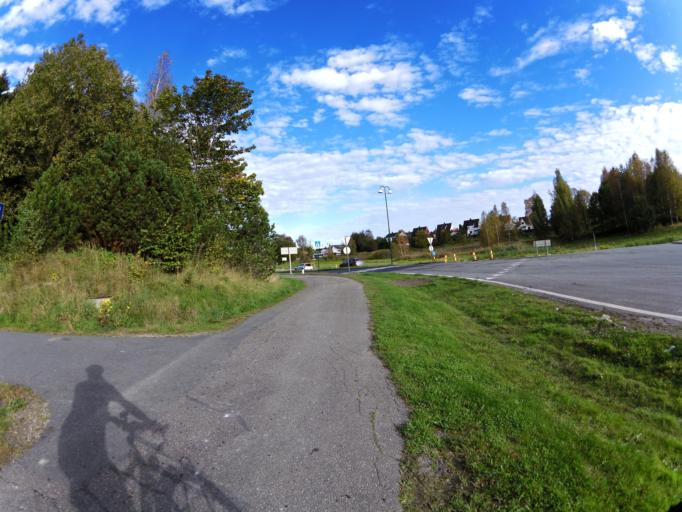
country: NO
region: Ostfold
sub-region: Sarpsborg
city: Sarpsborg
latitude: 59.2833
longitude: 11.0953
